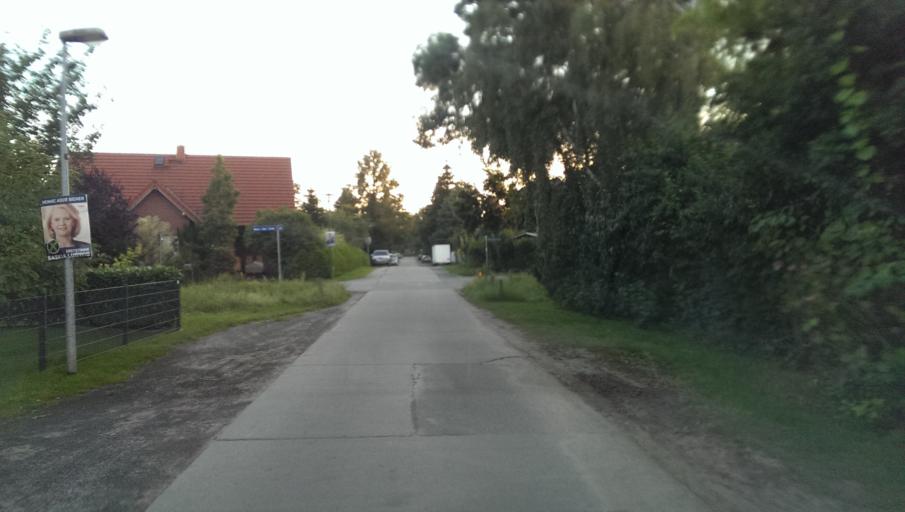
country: DE
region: Berlin
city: Lichterfelde
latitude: 52.4077
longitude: 13.2979
